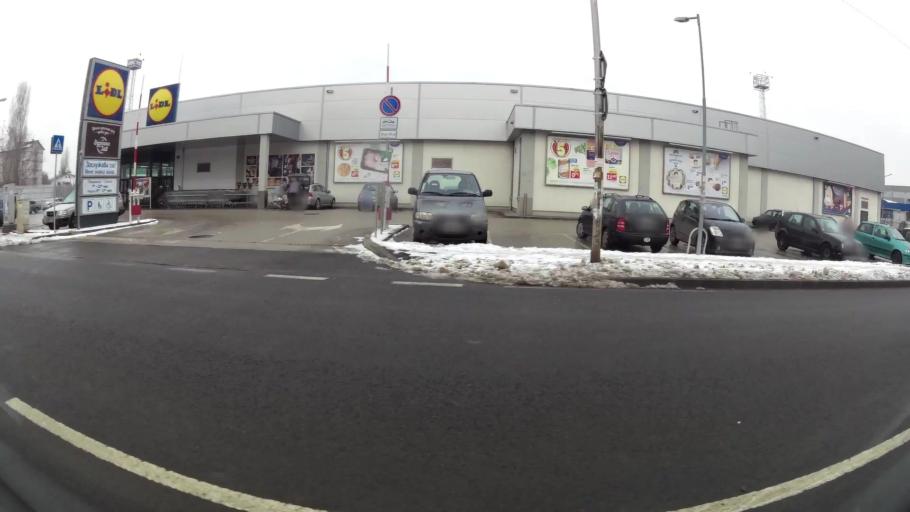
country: BG
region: Sofia-Capital
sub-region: Stolichna Obshtina
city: Sofia
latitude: 42.7083
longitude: 23.3430
